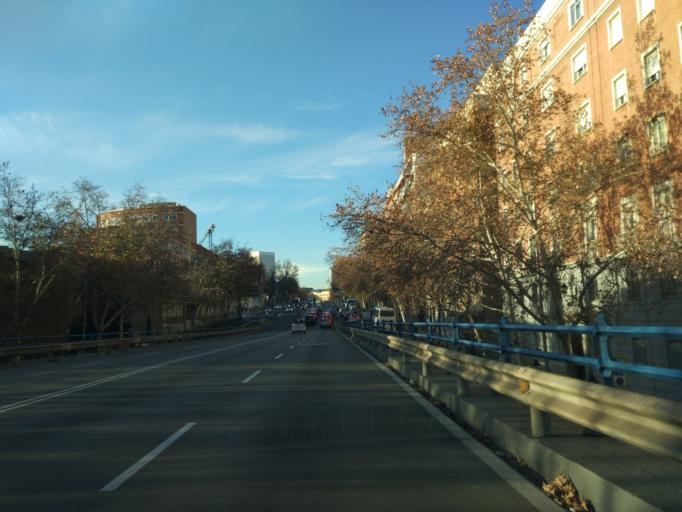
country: ES
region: Madrid
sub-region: Provincia de Madrid
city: Salamanca
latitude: 40.4408
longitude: -3.6809
